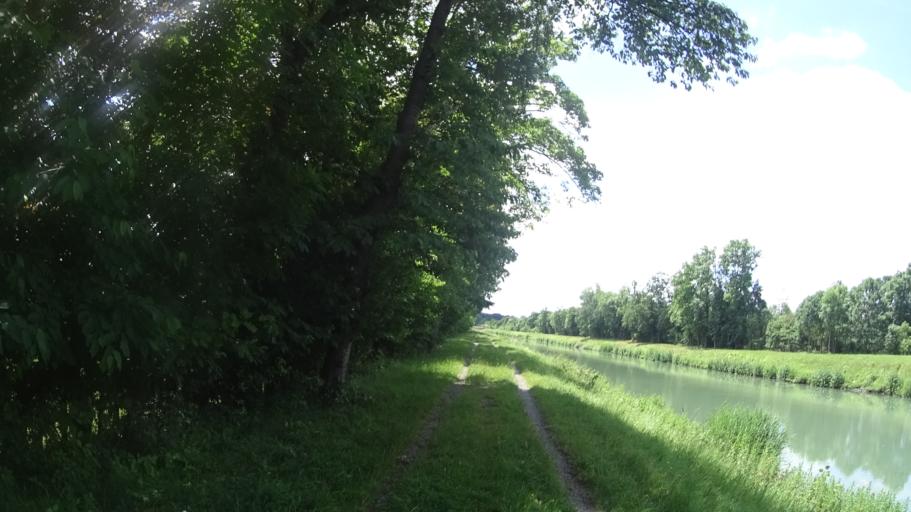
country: DE
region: Lower Saxony
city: Harsum
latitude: 52.2311
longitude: 9.9418
